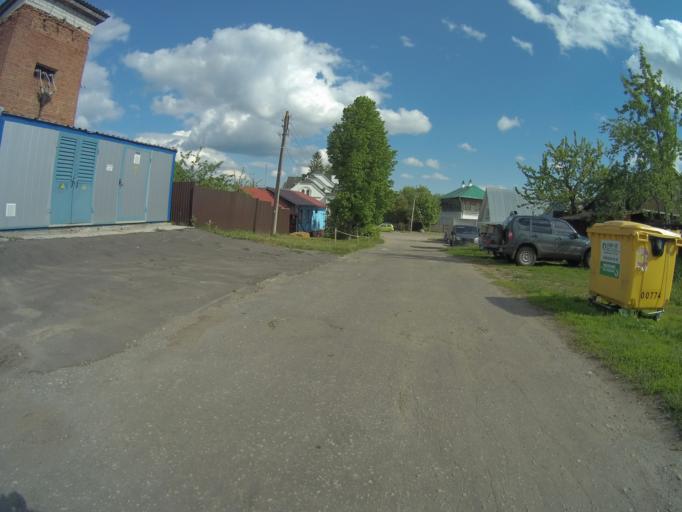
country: RU
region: Vladimir
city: Suzdal'
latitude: 56.4141
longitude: 40.4360
